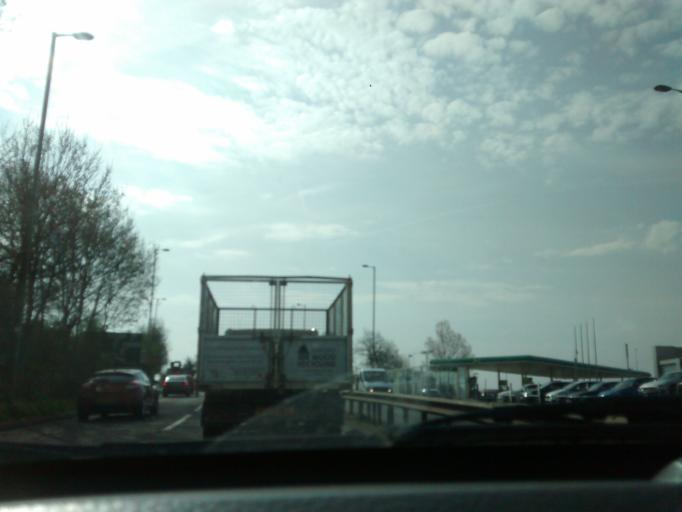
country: GB
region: England
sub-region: Oxfordshire
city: Yarnton
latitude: 51.7897
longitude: -1.2822
